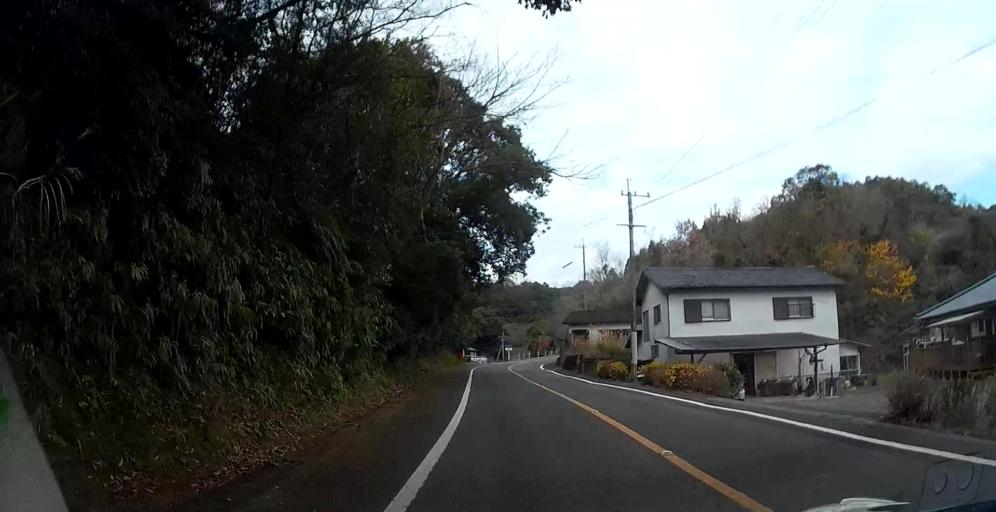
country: JP
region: Kumamoto
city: Minamata
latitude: 32.3629
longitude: 130.4949
